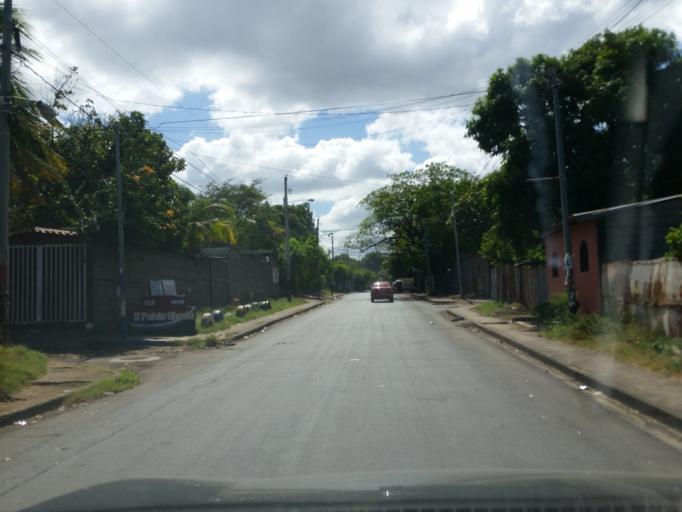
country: NI
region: Managua
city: Managua
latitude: 12.1182
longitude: -86.2321
